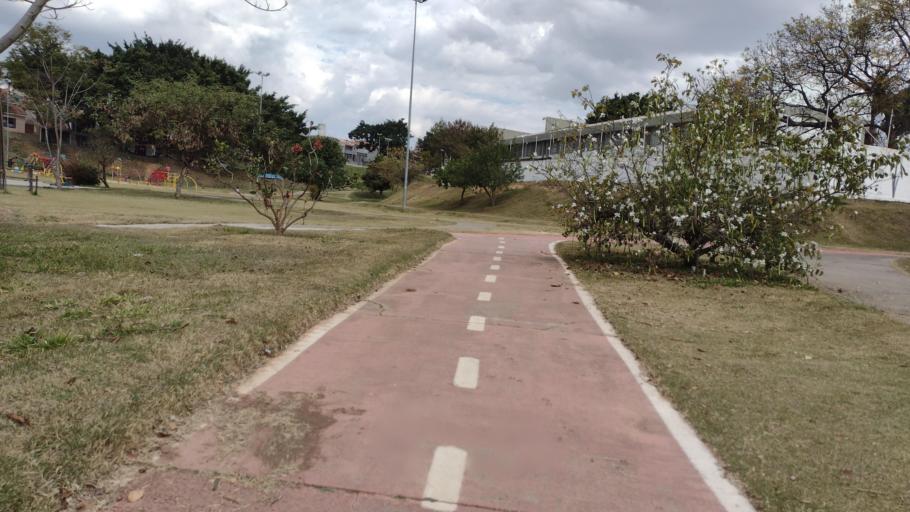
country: BR
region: Sao Paulo
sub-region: Sorocaba
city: Sorocaba
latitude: -23.4628
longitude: -47.4743
